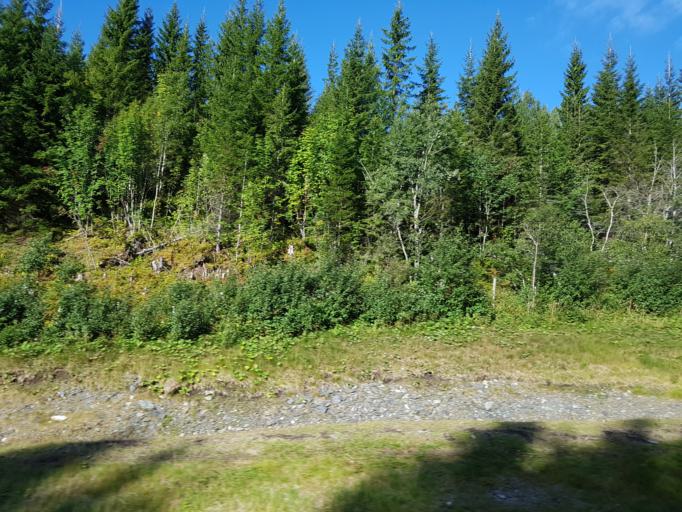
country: NO
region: Sor-Trondelag
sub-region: Trondheim
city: Trondheim
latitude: 63.6664
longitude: 10.2462
